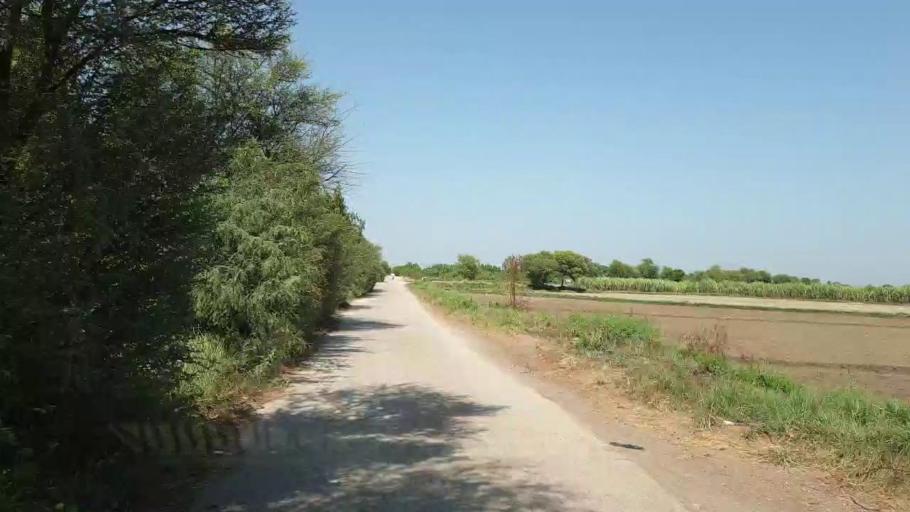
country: PK
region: Sindh
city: Tando Jam
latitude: 25.4814
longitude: 68.4628
